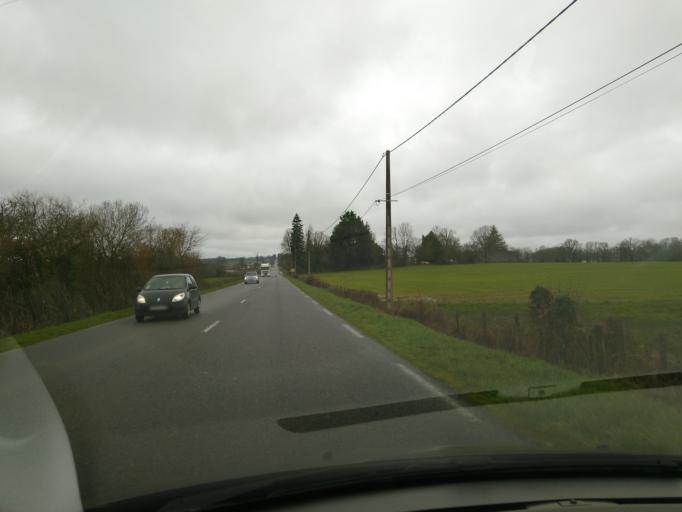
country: FR
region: Limousin
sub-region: Departement de la Haute-Vienne
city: Solignac
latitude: 45.7136
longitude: 1.2460
